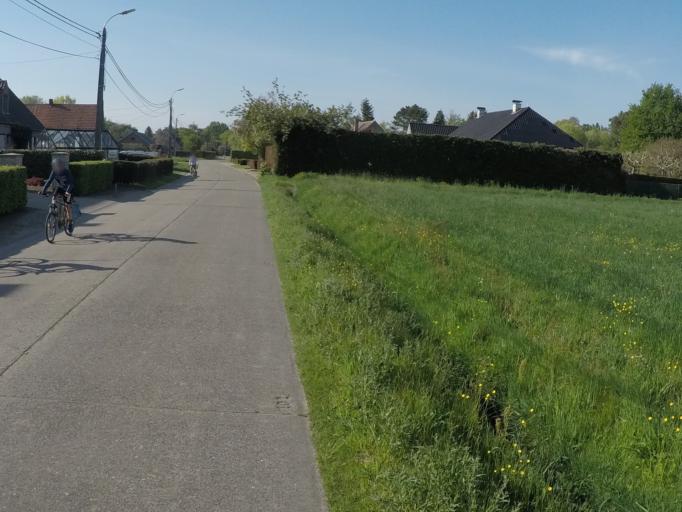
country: BE
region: Flanders
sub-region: Provincie Antwerpen
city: Nijlen
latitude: 51.1497
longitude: 4.6373
